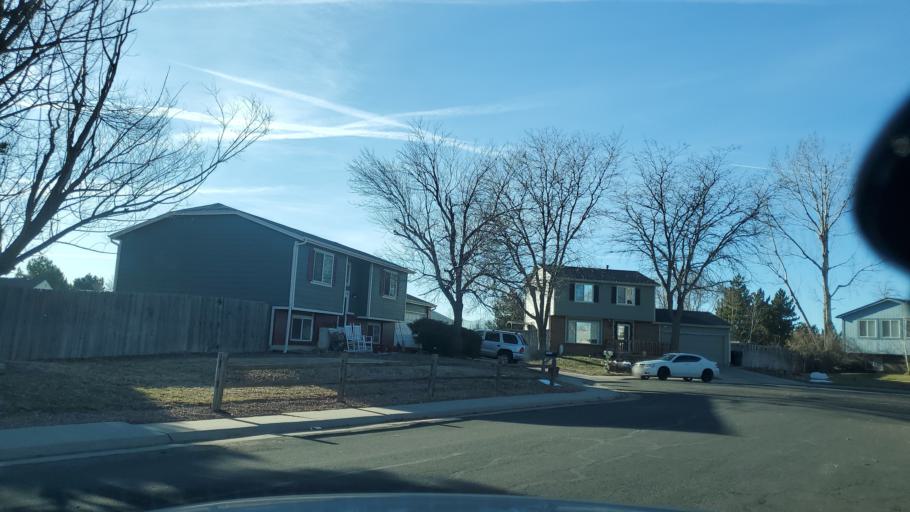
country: US
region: Colorado
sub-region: Adams County
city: Thornton
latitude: 39.9073
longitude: -104.9394
